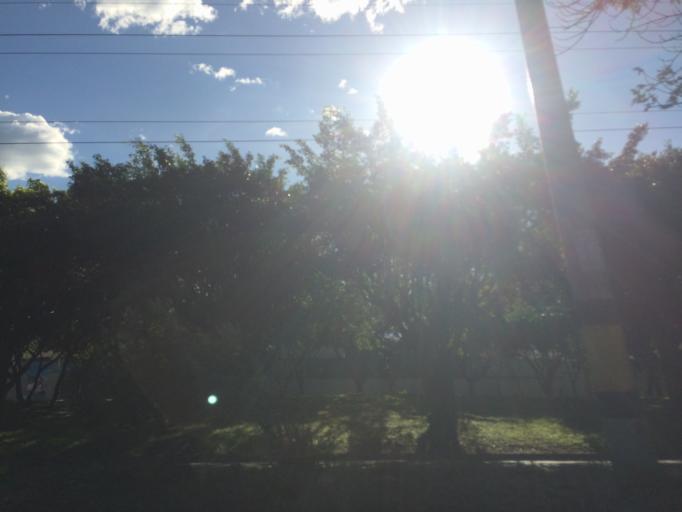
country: CO
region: Antioquia
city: Medellin
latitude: 6.2245
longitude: -75.5768
